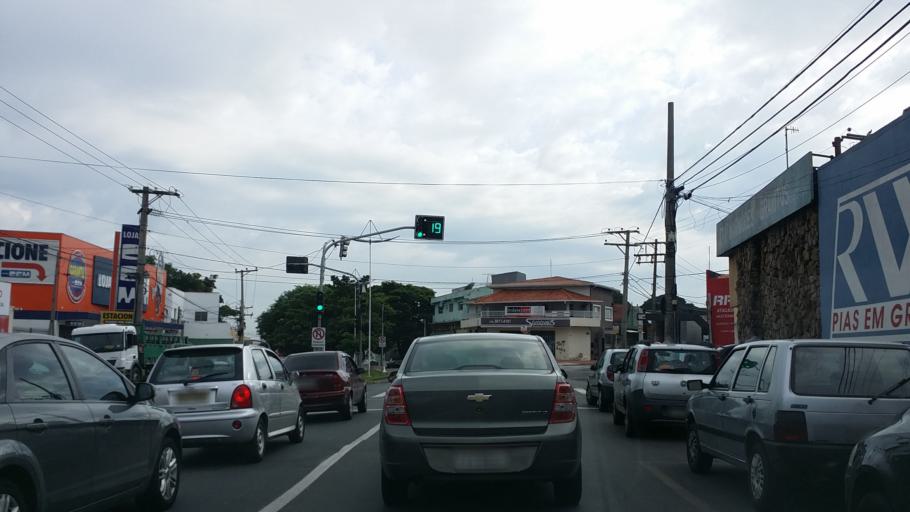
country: BR
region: Sao Paulo
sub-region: Indaiatuba
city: Indaiatuba
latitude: -23.1012
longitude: -47.2162
